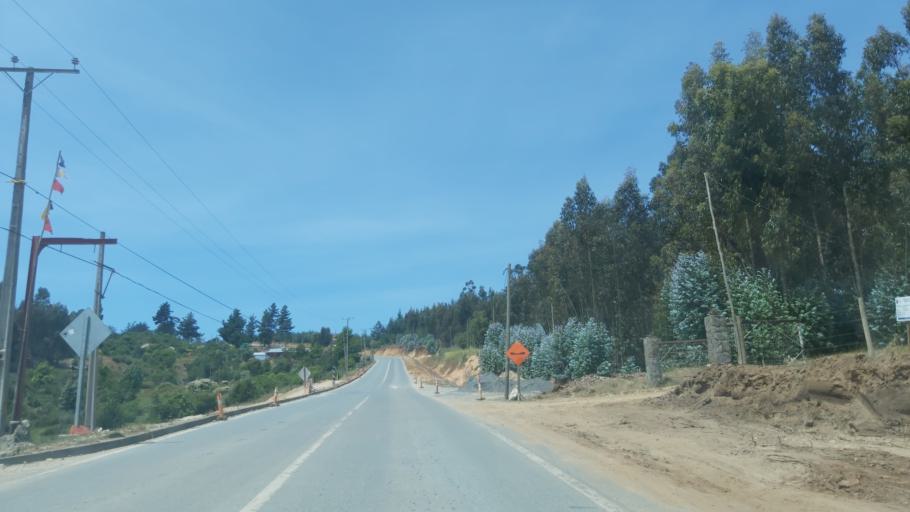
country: CL
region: Maule
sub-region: Provincia de Talca
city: Constitucion
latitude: -35.4433
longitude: -72.4616
